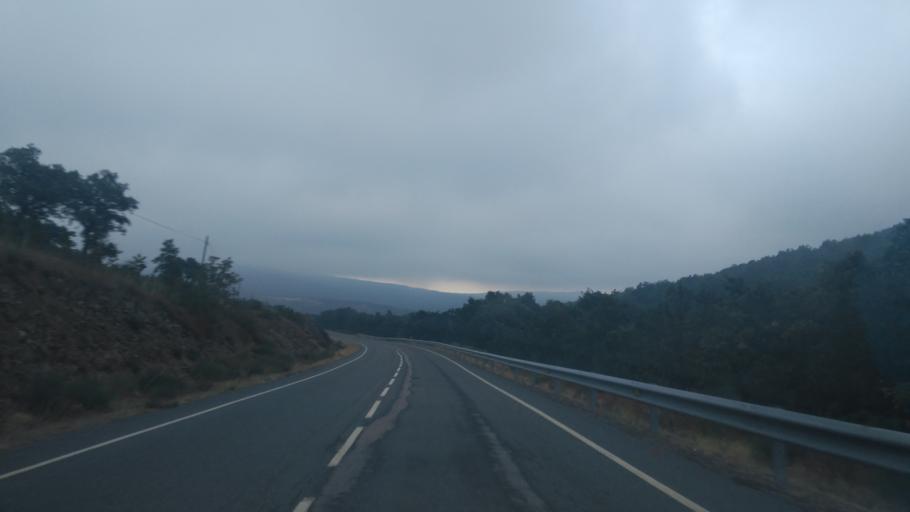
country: ES
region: Castille and Leon
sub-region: Provincia de Salamanca
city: Cereceda de la Sierra
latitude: 40.5868
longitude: -6.0874
